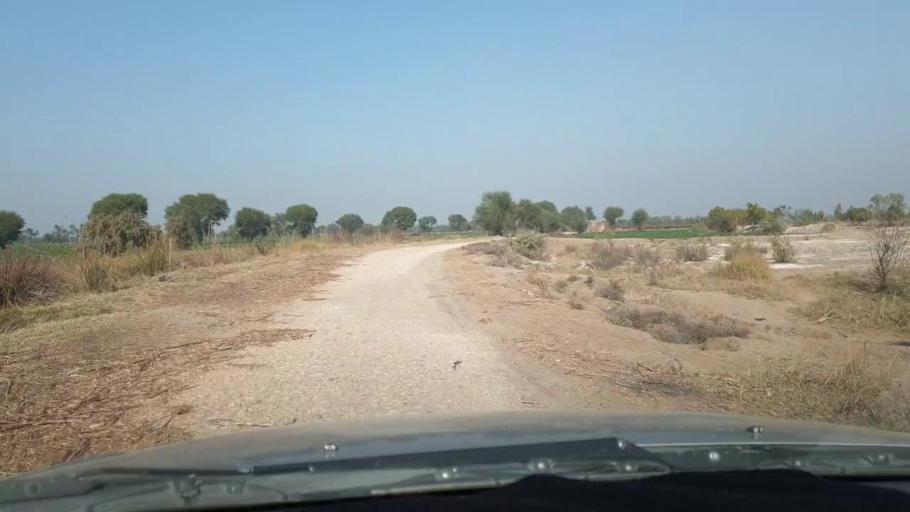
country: PK
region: Sindh
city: Mirpur Mathelo
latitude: 27.9265
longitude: 69.5612
